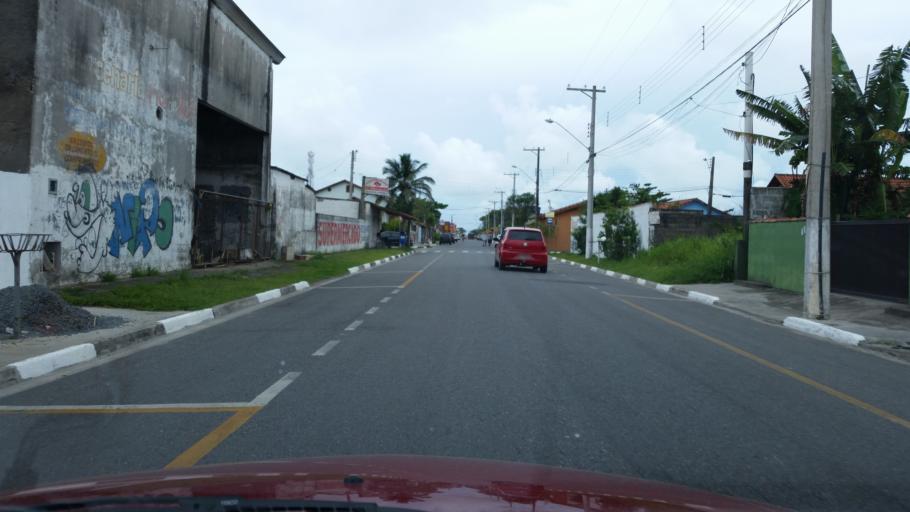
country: BR
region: Sao Paulo
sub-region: Iguape
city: Iguape
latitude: -24.7423
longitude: -47.5547
